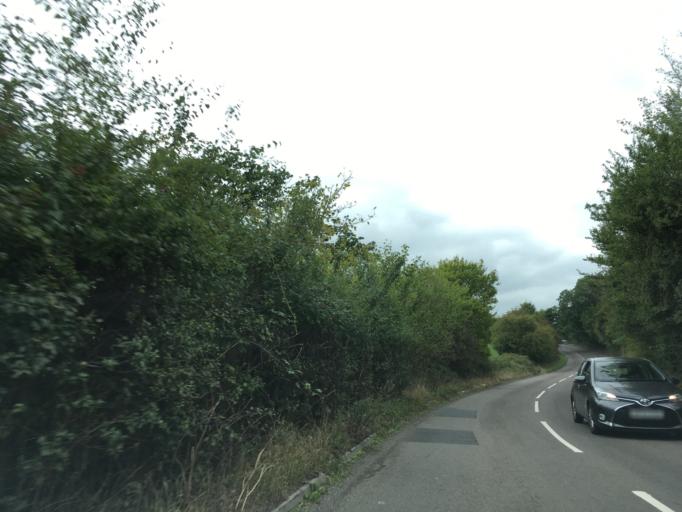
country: GB
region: England
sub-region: South Gloucestershire
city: Siston
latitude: 51.4603
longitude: -2.4611
